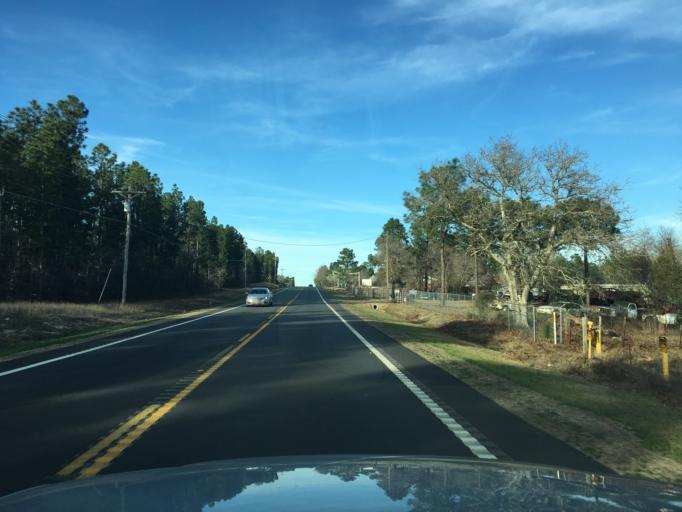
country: US
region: South Carolina
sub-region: Aiken County
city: Aiken
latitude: 33.6839
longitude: -81.6668
